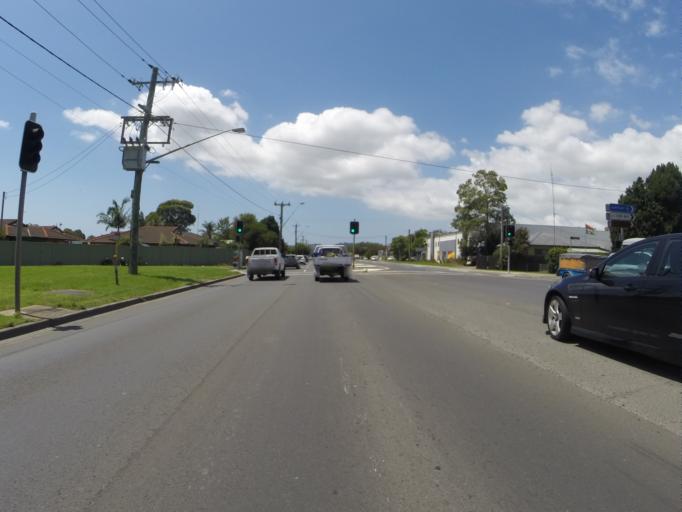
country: AU
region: New South Wales
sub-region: Shellharbour
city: Albion Park Rail
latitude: -34.5562
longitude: 150.7917
